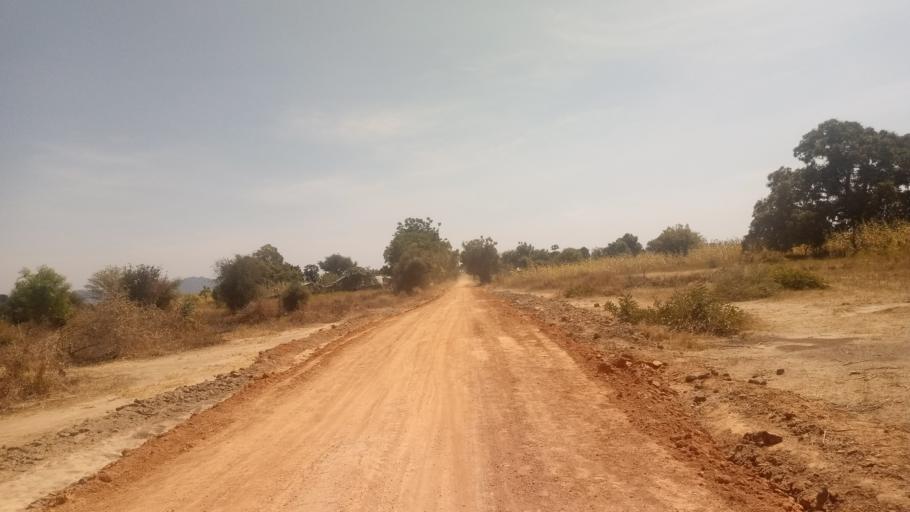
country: NG
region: Adamawa
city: Madagali
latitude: 10.8514
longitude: 13.3910
